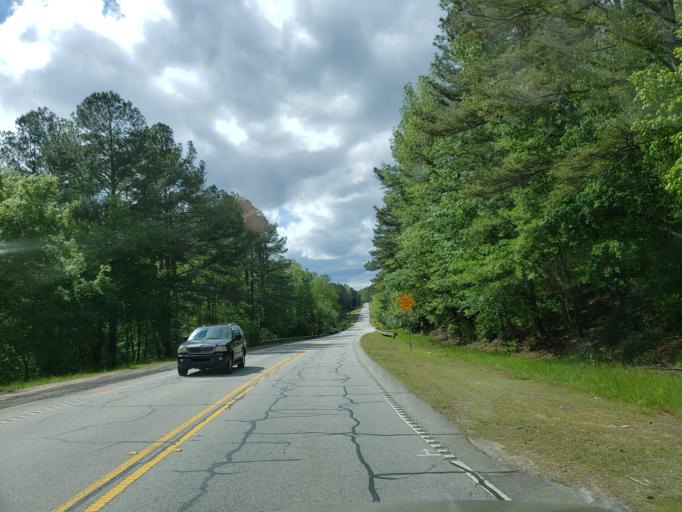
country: US
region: Georgia
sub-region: Haralson County
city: Tallapoosa
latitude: 33.7405
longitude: -85.3343
